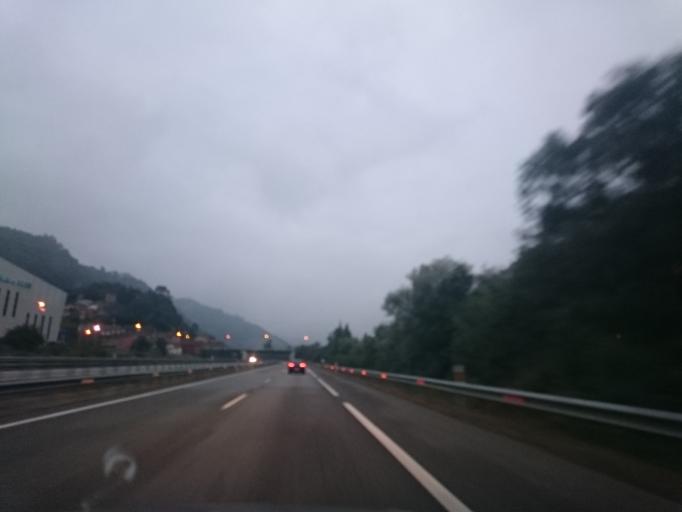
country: ES
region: Asturias
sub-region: Province of Asturias
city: Mieres
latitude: 43.2255
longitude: -5.7840
